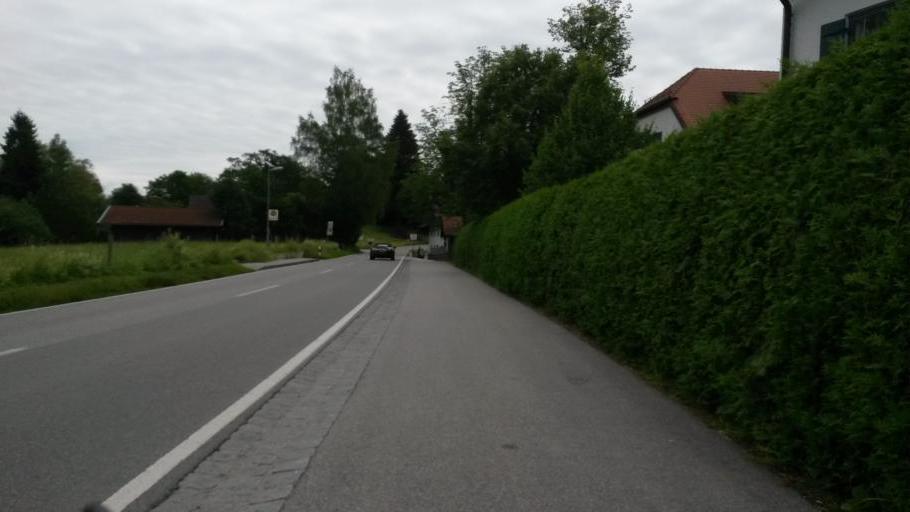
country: DE
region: Bavaria
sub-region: Upper Bavaria
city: Rimsting
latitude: 47.8890
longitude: 12.3546
